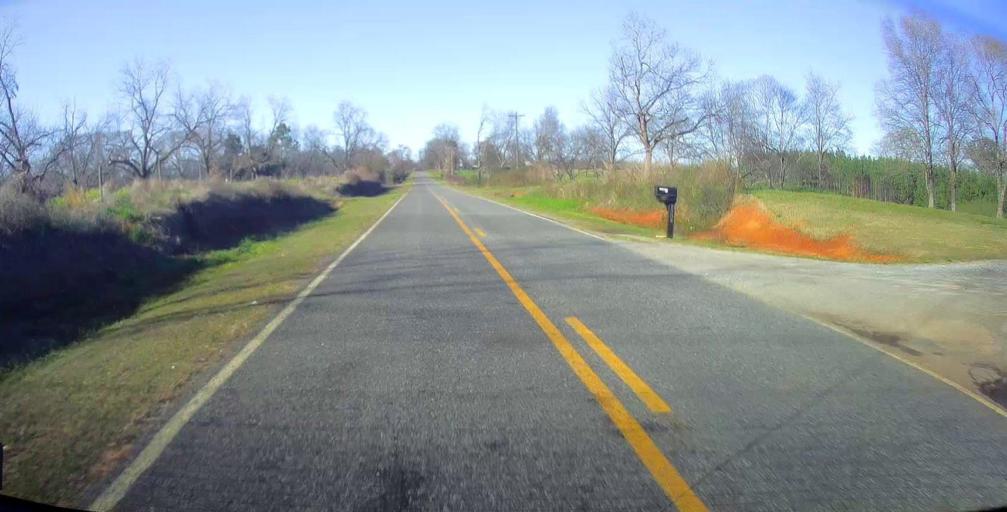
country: US
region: Georgia
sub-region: Peach County
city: Fort Valley
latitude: 32.6118
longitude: -83.8522
